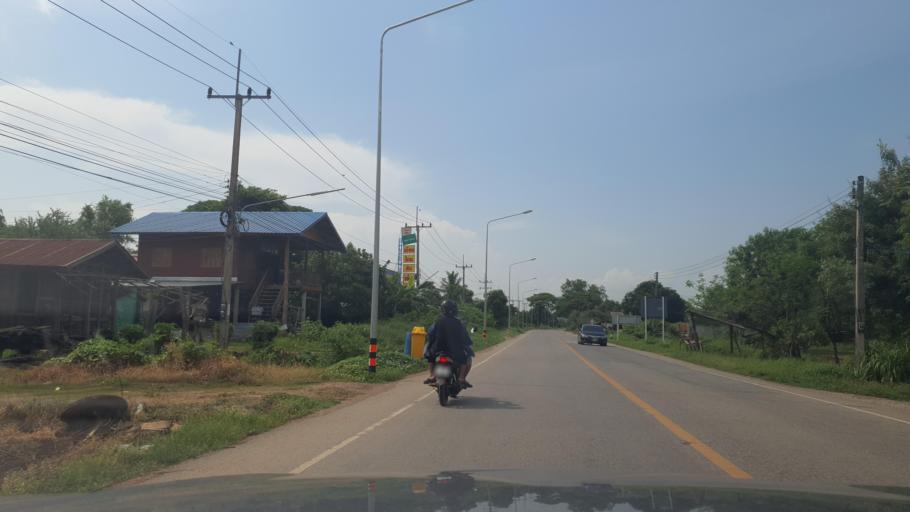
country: TH
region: Sukhothai
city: Si Samrong
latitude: 17.0896
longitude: 99.8837
